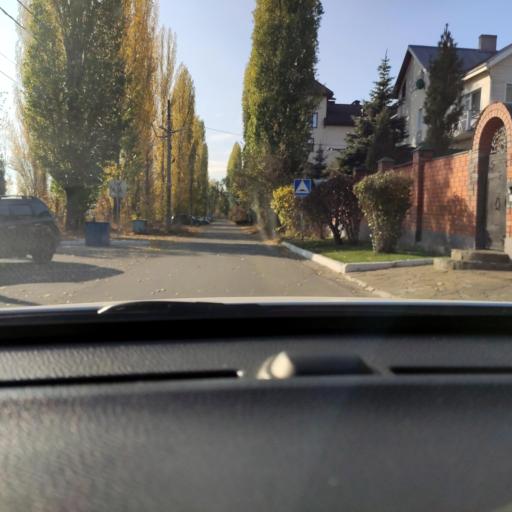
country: RU
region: Voronezj
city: Voronezh
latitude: 51.6999
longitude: 39.2362
